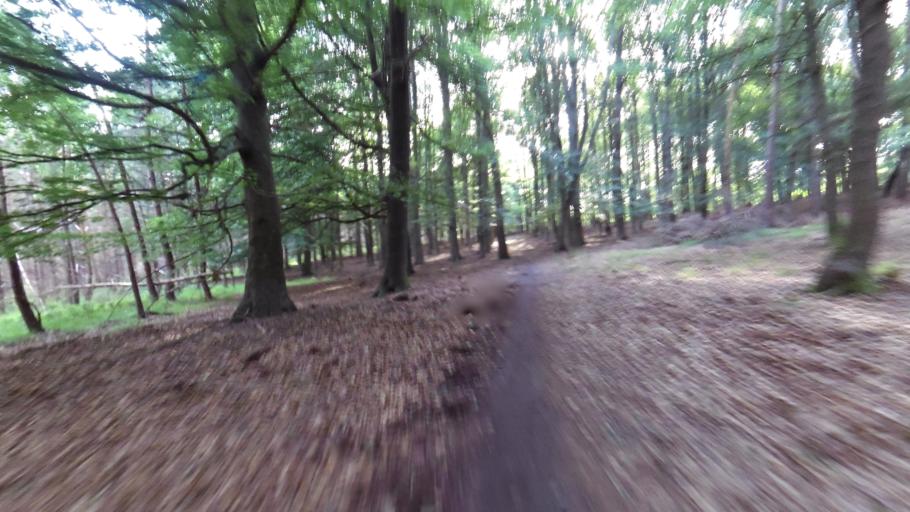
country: NL
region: Gelderland
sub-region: Gemeente Apeldoorn
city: Uddel
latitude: 52.2199
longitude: 5.8457
